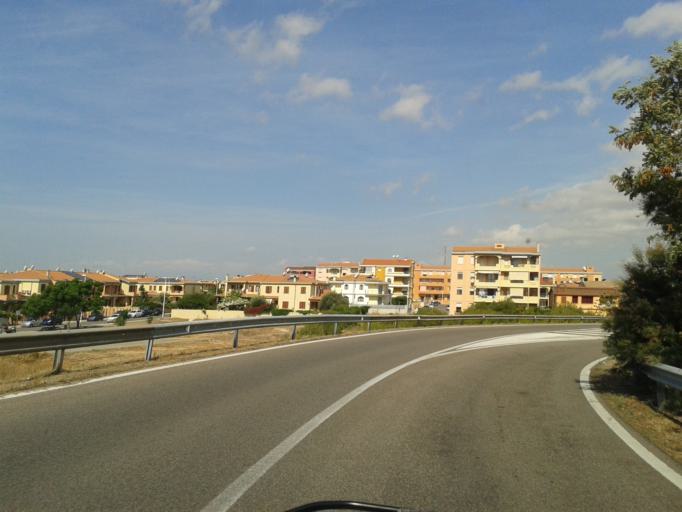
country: IT
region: Sardinia
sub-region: Provincia di Cagliari
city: Quartucciu
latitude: 39.2550
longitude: 9.1900
